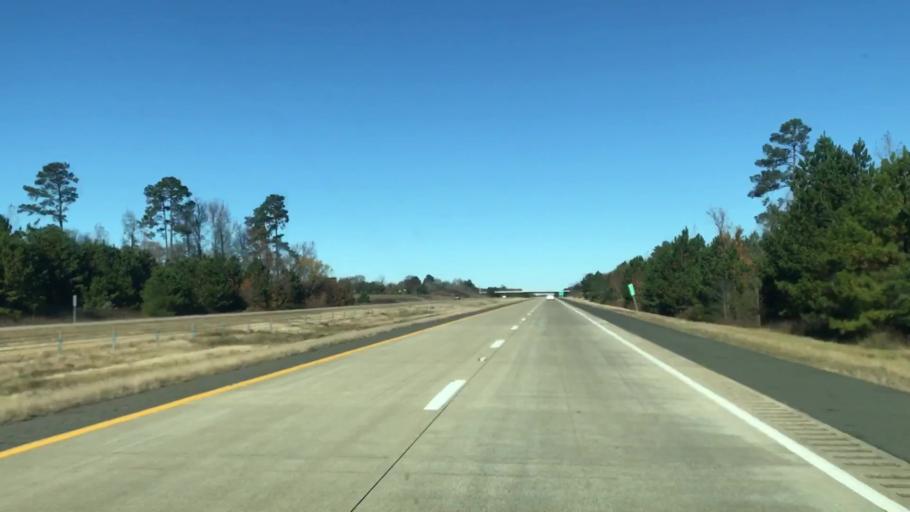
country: US
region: Texas
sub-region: Bowie County
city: Texarkana
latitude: 33.3106
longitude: -93.9397
